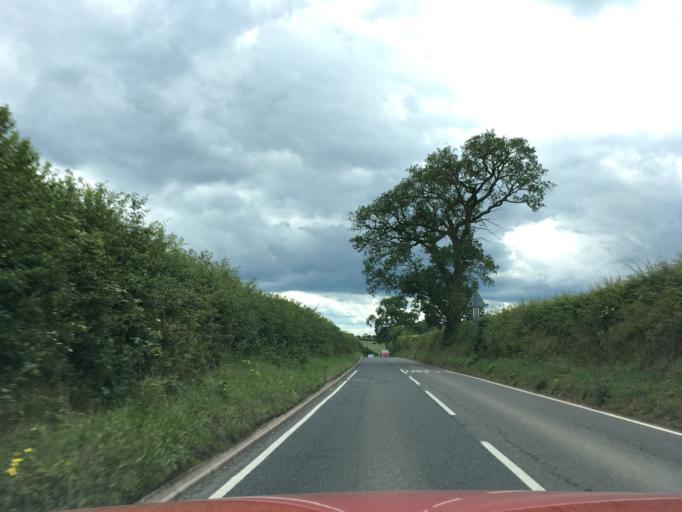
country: GB
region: England
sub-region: Central Bedfordshire
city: Woburn
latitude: 51.9792
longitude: -0.6382
